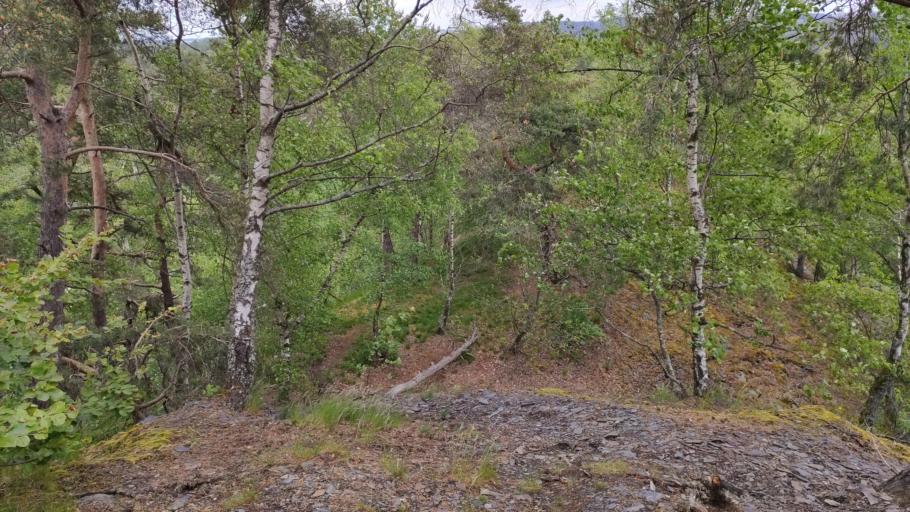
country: DE
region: Bavaria
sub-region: Upper Franconia
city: Ludwigsstadt
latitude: 50.4807
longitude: 11.4561
